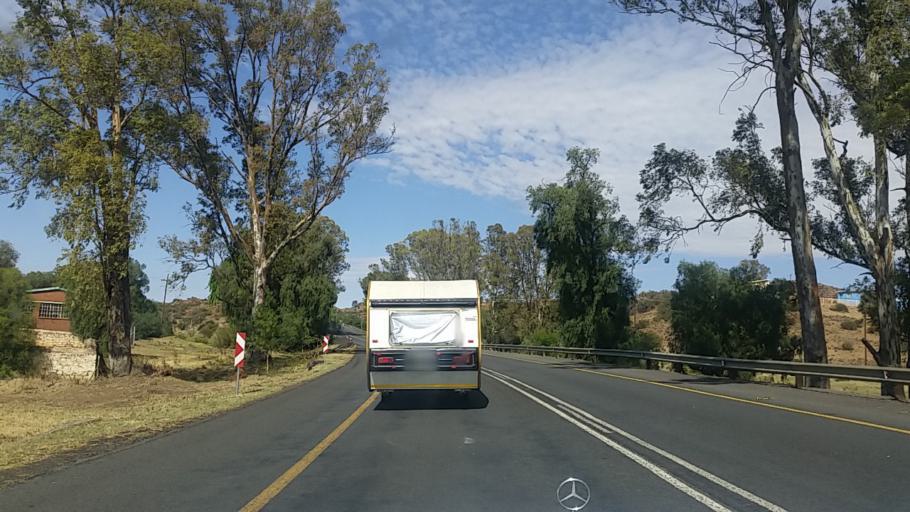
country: ZA
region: Northern Cape
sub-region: Pixley ka Seme District Municipality
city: Colesberg
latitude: -30.7116
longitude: 25.1013
